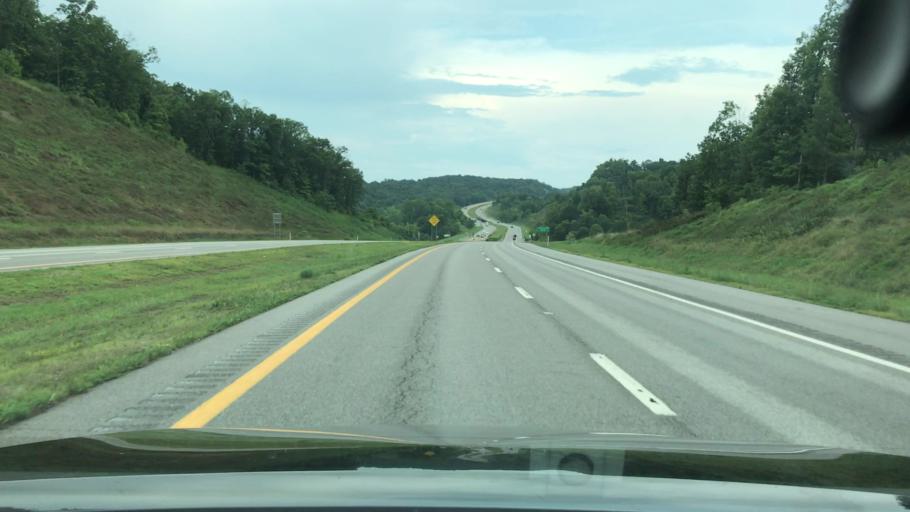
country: US
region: West Virginia
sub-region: Mason County
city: Point Pleasant
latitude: 38.7837
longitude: -82.0757
